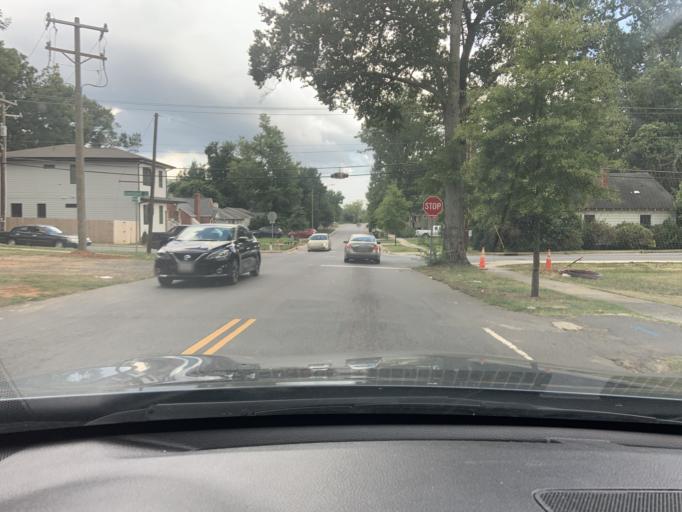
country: US
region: North Carolina
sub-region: Mecklenburg County
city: Charlotte
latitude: 35.2265
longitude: -80.8844
